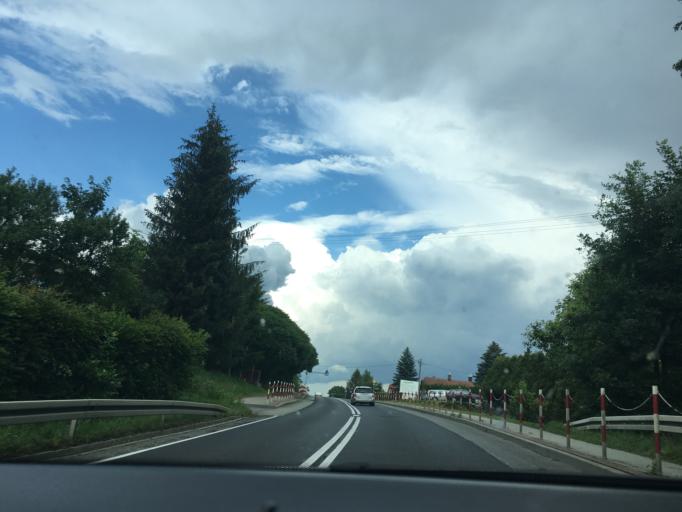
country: PL
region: Subcarpathian Voivodeship
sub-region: Powiat krosnienski
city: Kroscienko Wyzne
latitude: 49.6575
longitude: 21.8327
